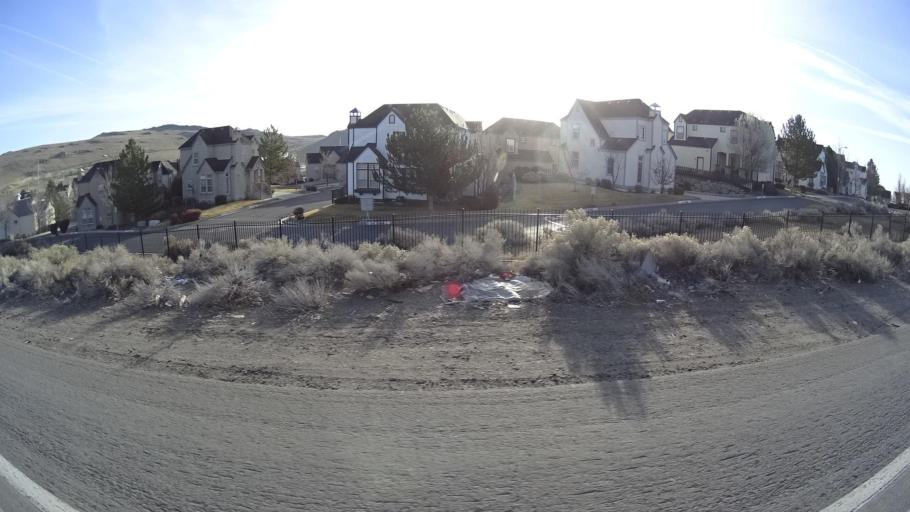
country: US
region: Nevada
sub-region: Washoe County
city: Sparks
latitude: 39.5620
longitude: -119.7738
